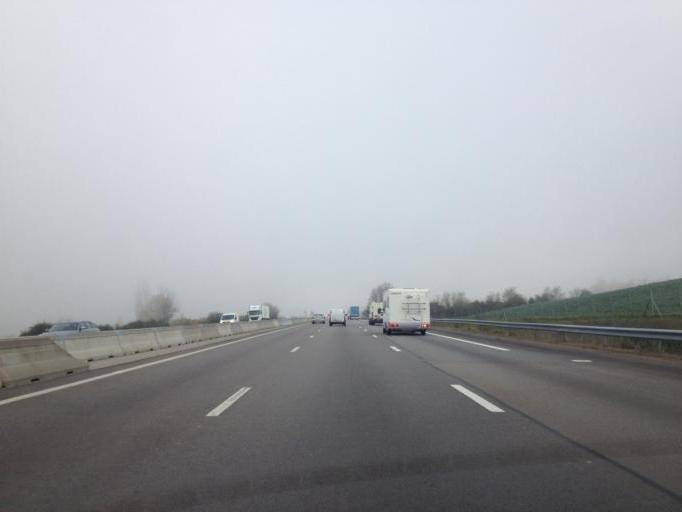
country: FR
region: Rhone-Alpes
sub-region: Departement de la Drome
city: Savasse
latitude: 44.6163
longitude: 4.7929
